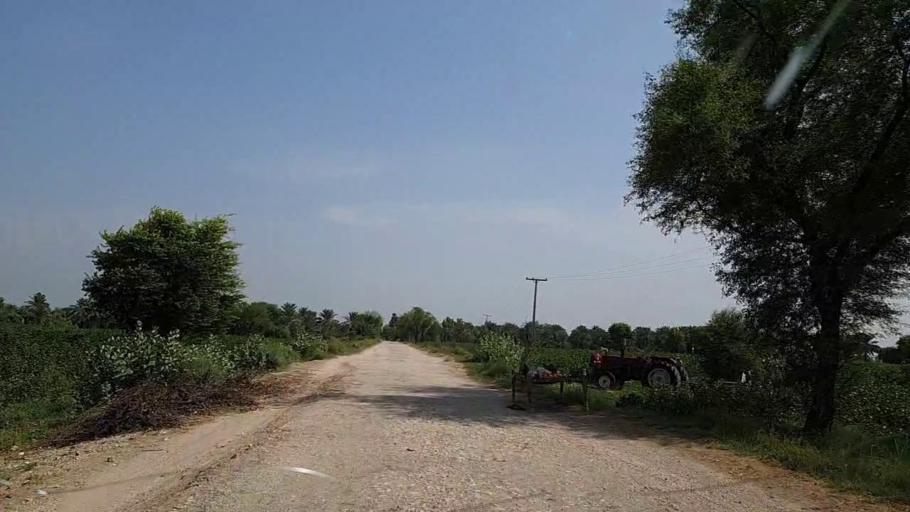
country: PK
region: Sindh
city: Khanpur
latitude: 27.7874
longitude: 69.3188
